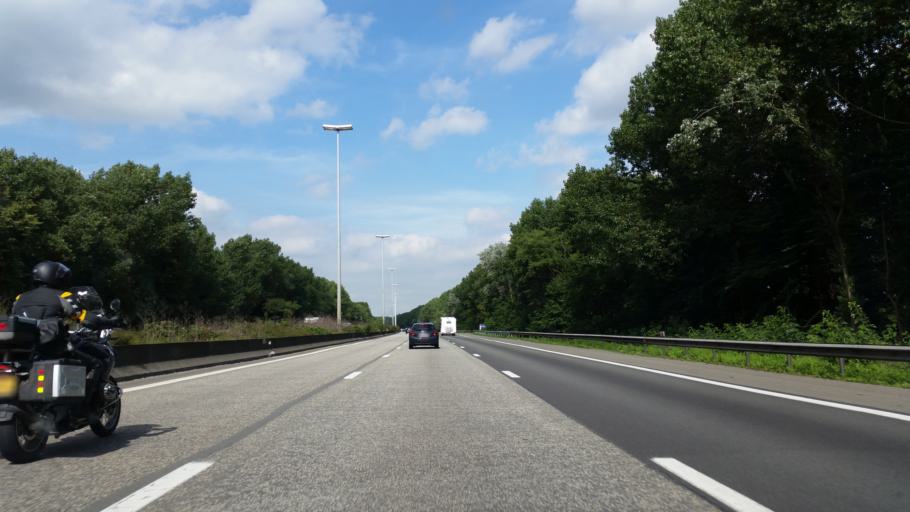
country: BE
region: Flanders
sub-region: Provincie Oost-Vlaanderen
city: Waasmunster
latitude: 51.1075
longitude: 4.0536
